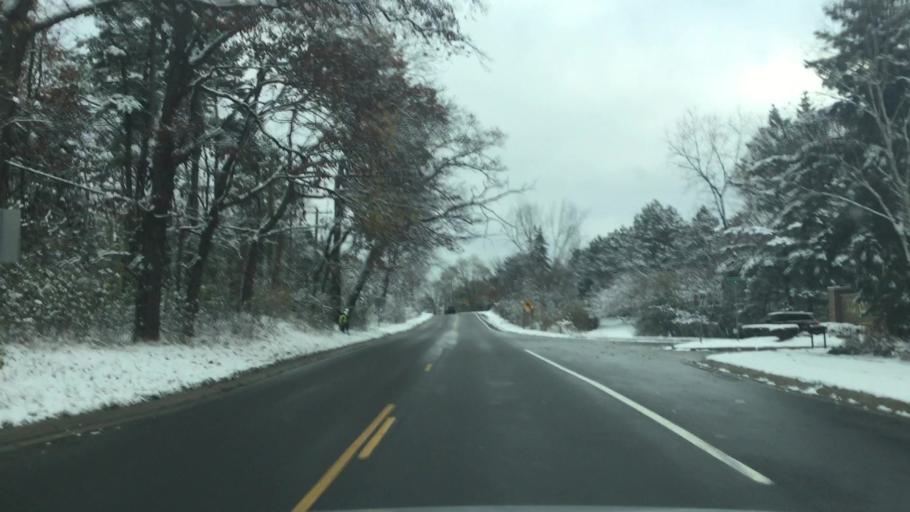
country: US
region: Michigan
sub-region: Oakland County
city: West Bloomfield Township
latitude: 42.5715
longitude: -83.3815
